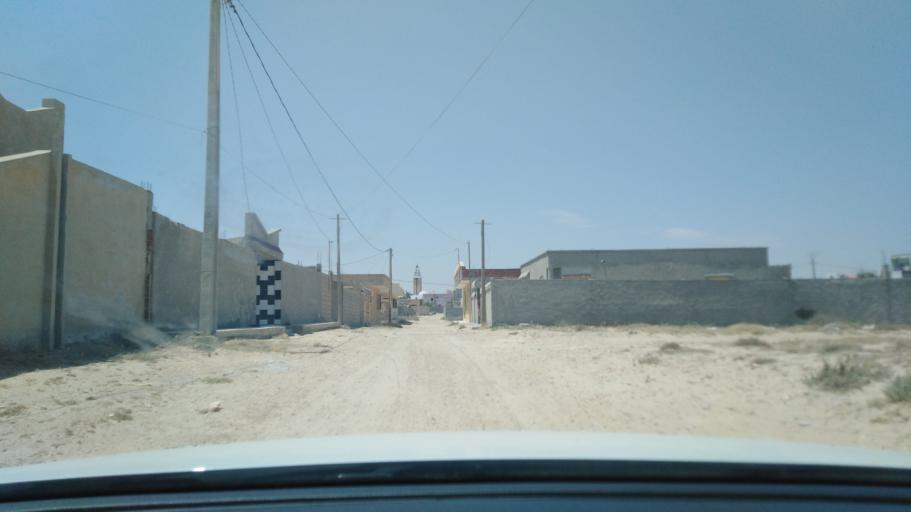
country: TN
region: Qabis
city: Gabes
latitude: 33.9483
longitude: 10.0733
